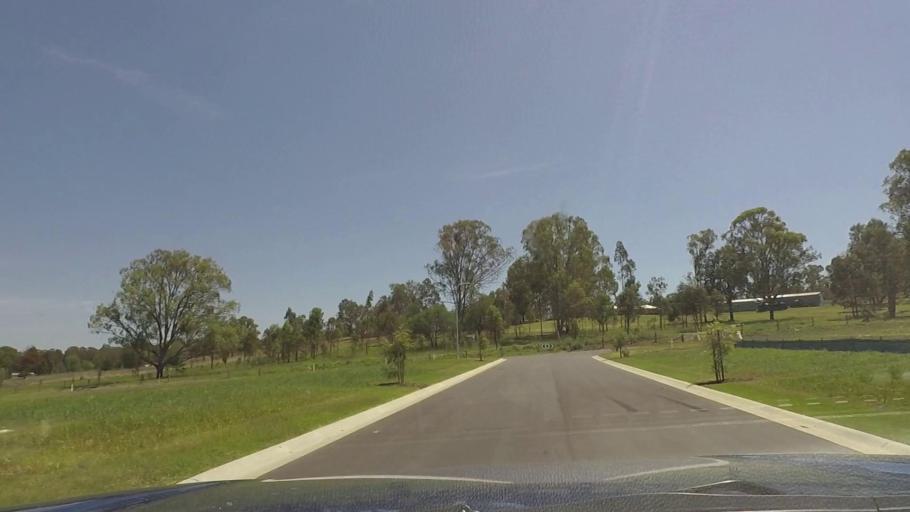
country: AU
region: Queensland
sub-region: Logan
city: Cedar Vale
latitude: -27.8872
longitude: 152.9882
